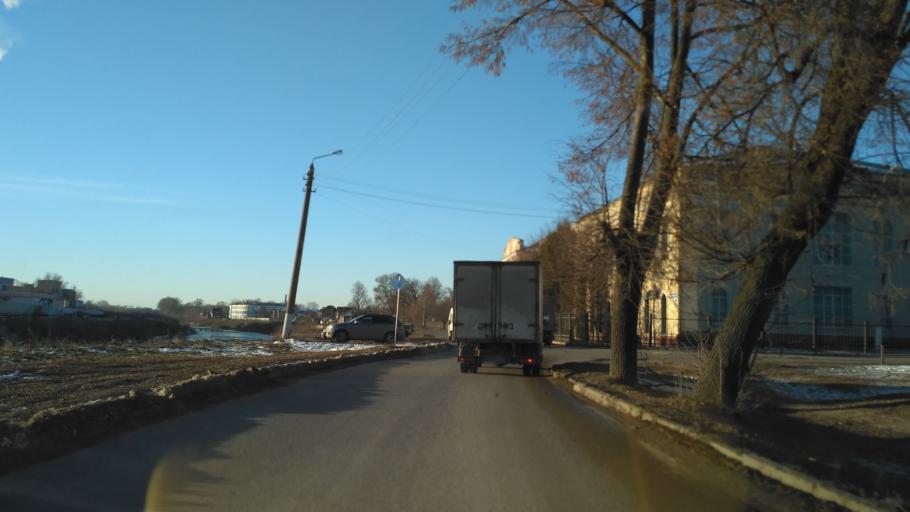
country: RU
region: Tula
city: Tula
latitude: 54.2043
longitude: 37.6130
